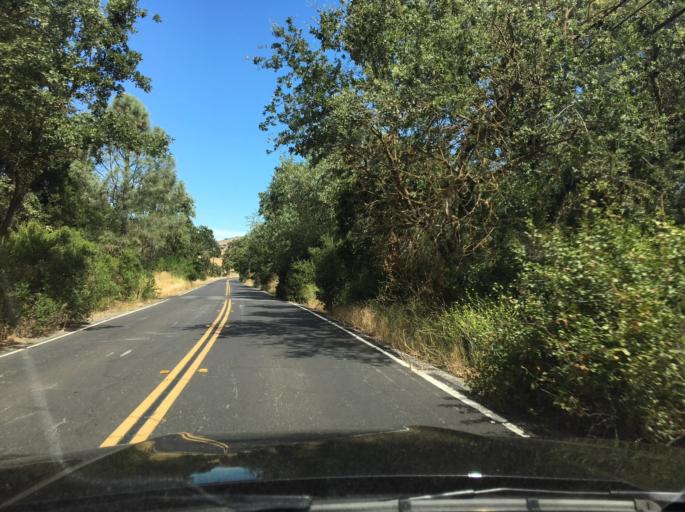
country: US
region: California
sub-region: Santa Clara County
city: Morgan Hill
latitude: 37.1695
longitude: -121.7565
